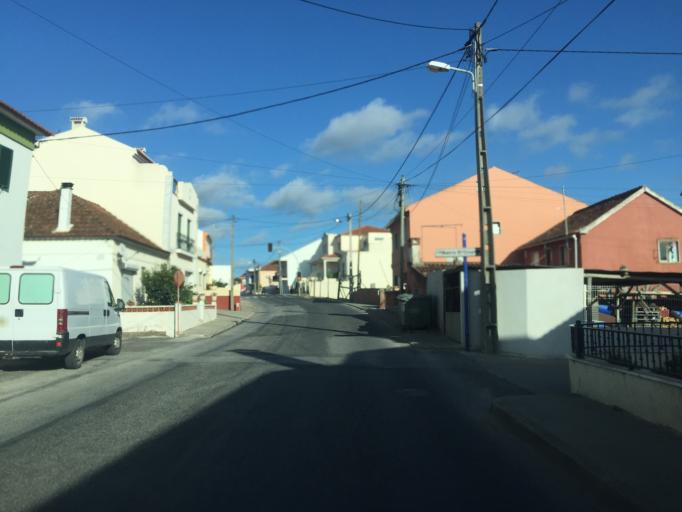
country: PT
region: Lisbon
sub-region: Torres Vedras
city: A dos Cunhados
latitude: 39.1492
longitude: -9.2950
